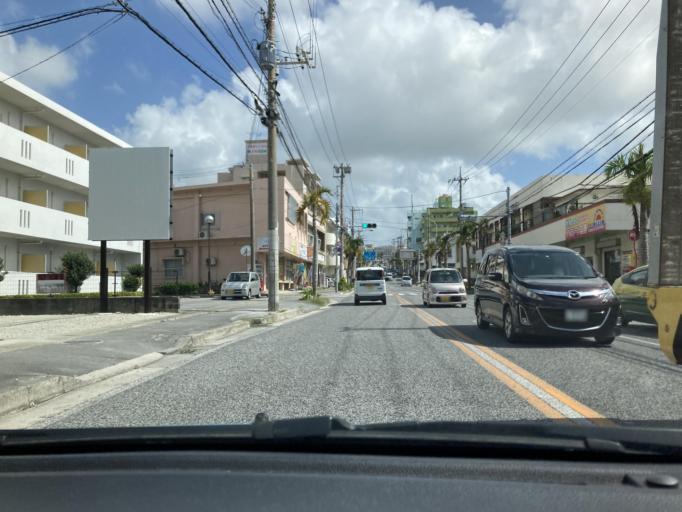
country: JP
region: Okinawa
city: Ginowan
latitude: 26.2681
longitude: 127.7342
